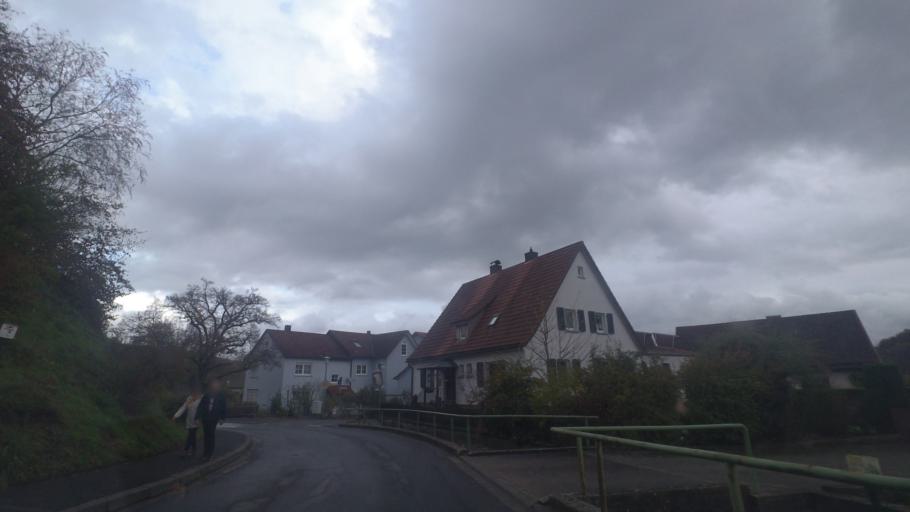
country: DE
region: Bavaria
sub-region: Regierungsbezirk Unterfranken
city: Oberelsbach
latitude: 50.3792
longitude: 10.1030
